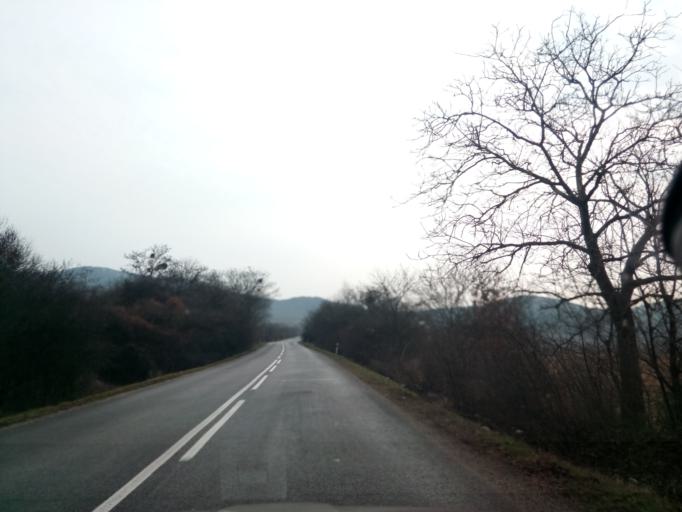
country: SK
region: Kosicky
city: Kosice
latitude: 48.6477
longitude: 21.4123
